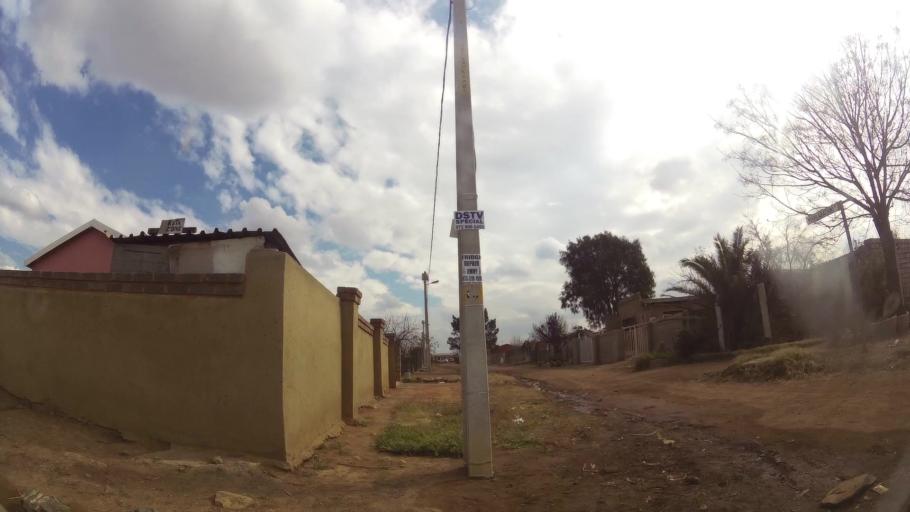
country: ZA
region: Gauteng
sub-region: Ekurhuleni Metropolitan Municipality
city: Germiston
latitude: -26.4072
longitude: 28.1663
